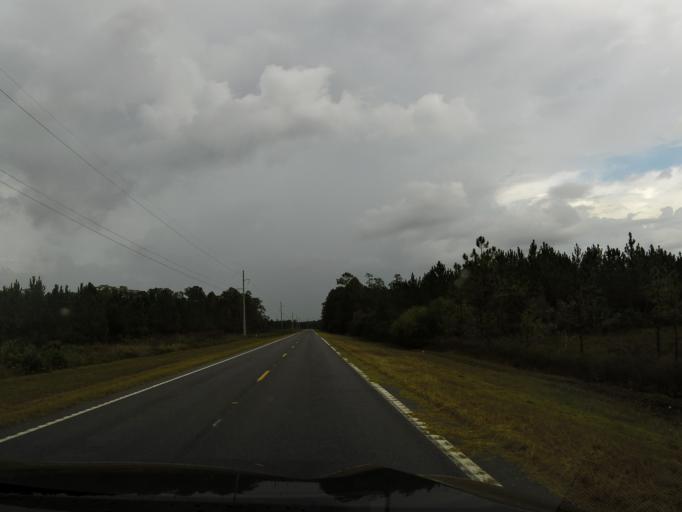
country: US
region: Florida
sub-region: Duval County
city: Baldwin
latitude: 30.4787
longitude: -82.0477
